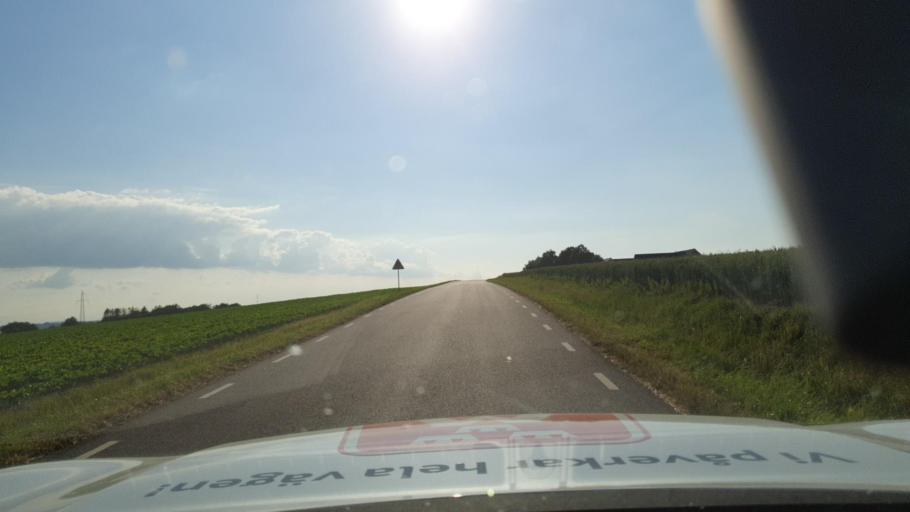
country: SE
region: Skane
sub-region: Skurups Kommun
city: Rydsgard
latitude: 55.5032
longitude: 13.5772
